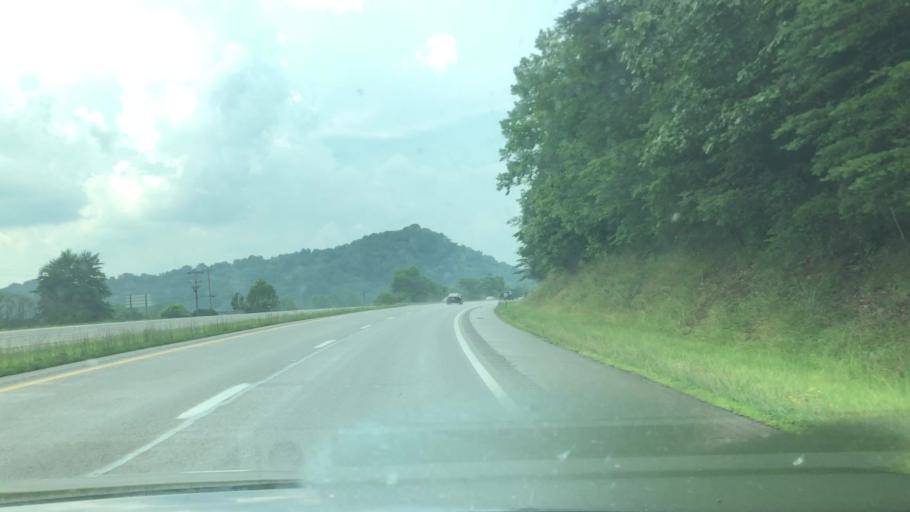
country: US
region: Ohio
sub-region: Jackson County
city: Jackson
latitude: 39.1427
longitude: -82.7251
